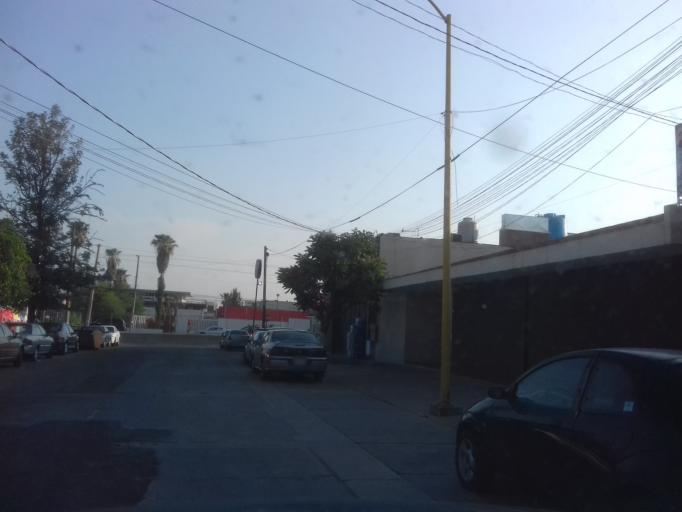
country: MX
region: Aguascalientes
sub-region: Aguascalientes
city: Aguascalientes
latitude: 21.8650
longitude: -102.2917
